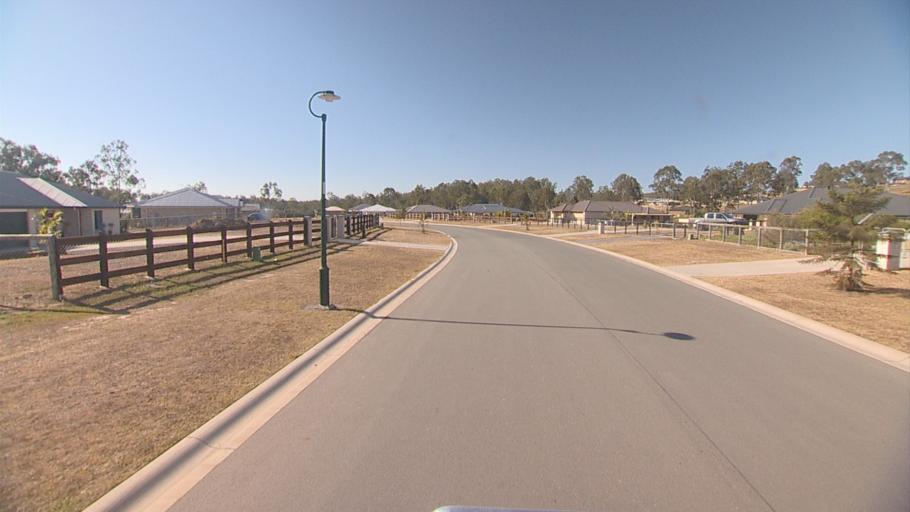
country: AU
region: Queensland
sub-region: Logan
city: Cedar Vale
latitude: -27.8719
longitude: 153.0470
